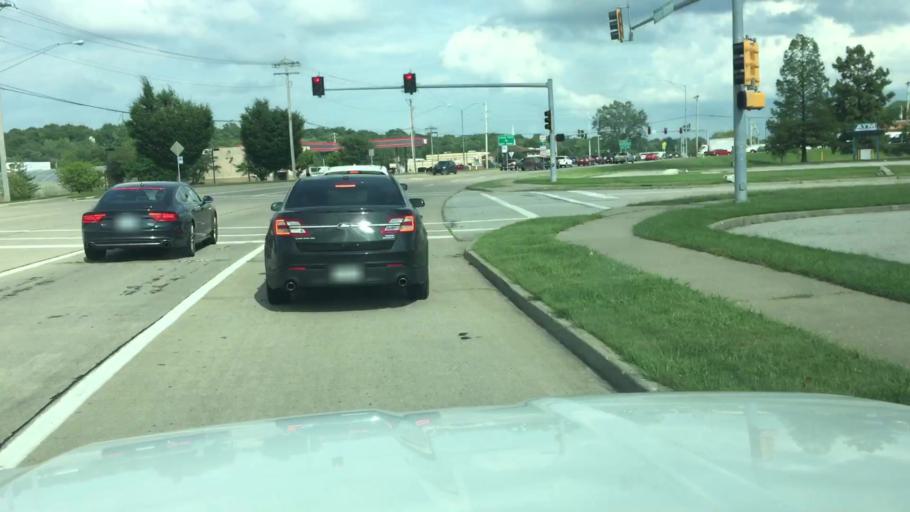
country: US
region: Missouri
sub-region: Jefferson County
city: Arnold
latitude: 38.4651
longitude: -90.3593
